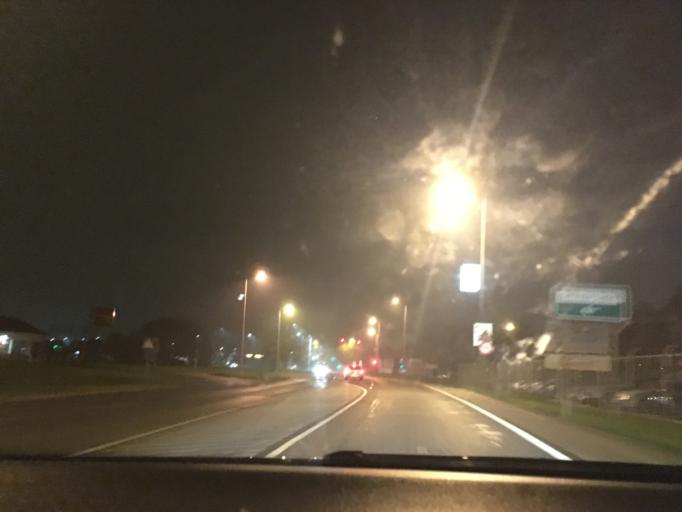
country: HU
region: Hajdu-Bihar
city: Debrecen
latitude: 47.5134
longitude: 21.6043
